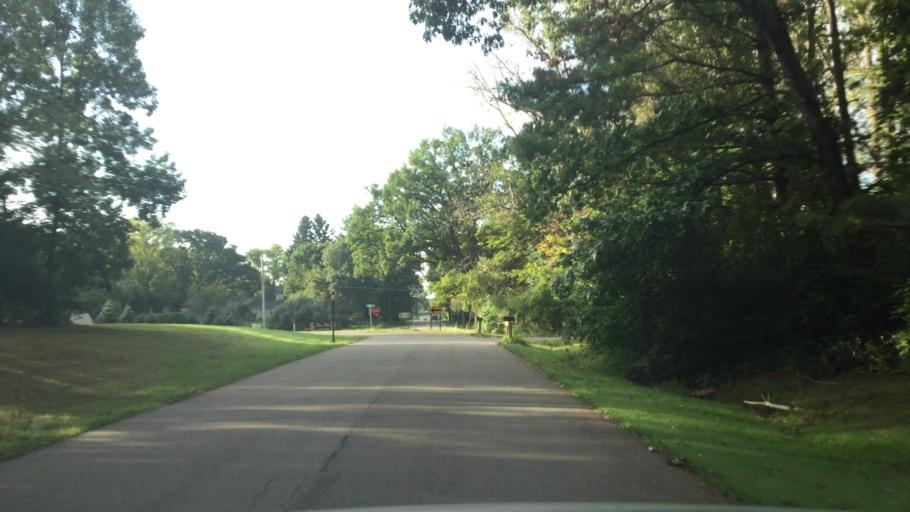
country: US
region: Michigan
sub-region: Livingston County
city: Whitmore Lake
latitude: 42.4619
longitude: -83.7992
